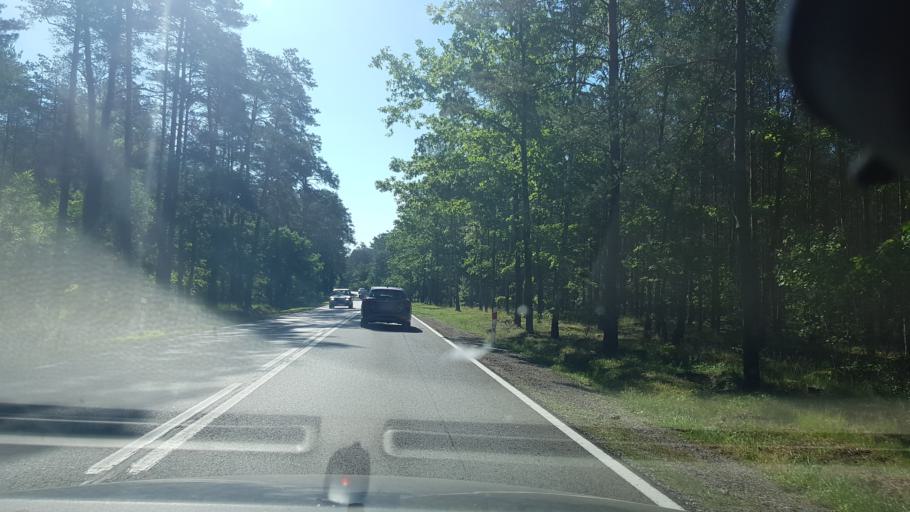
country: PL
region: Masovian Voivodeship
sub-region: Powiat wyszkowski
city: Branszczyk
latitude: 52.5585
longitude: 21.5816
